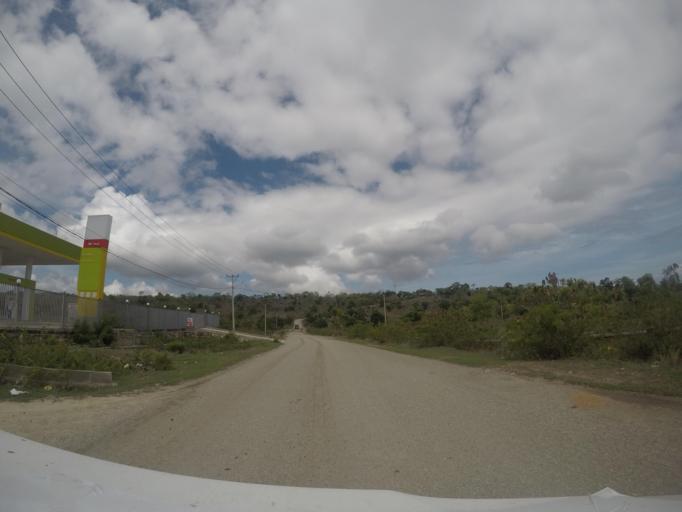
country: TL
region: Baucau
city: Baucau
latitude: -8.4704
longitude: 126.4366
